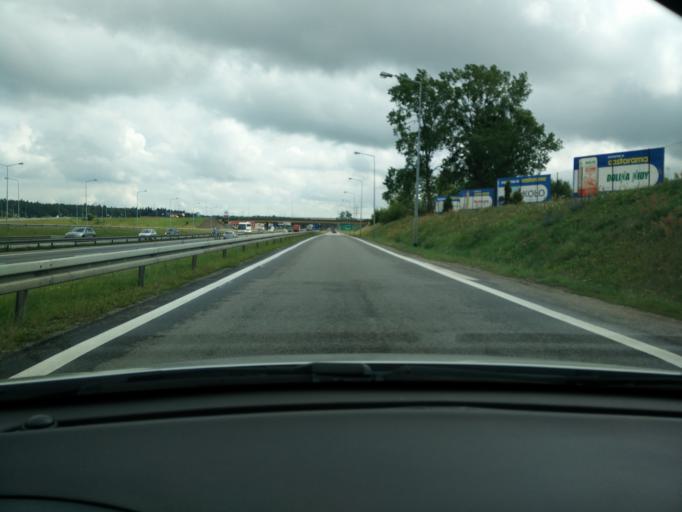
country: PL
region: Pomeranian Voivodeship
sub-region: Gdynia
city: Wielki Kack
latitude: 54.4324
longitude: 18.4874
